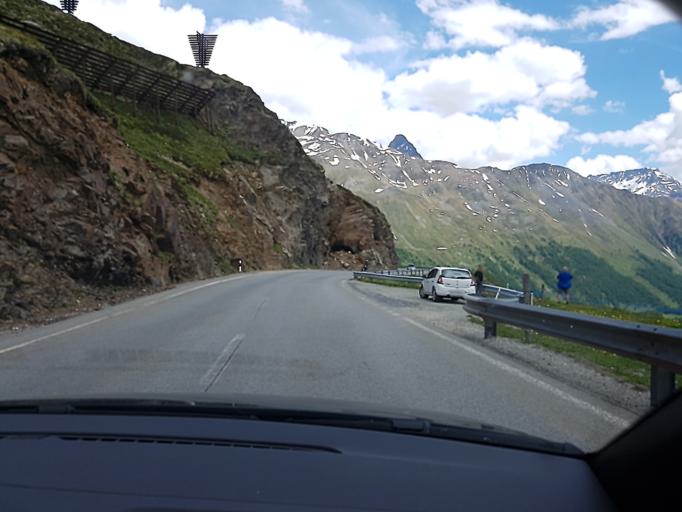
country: CH
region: Grisons
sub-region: Bernina District
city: Poschiavo
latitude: 46.4114
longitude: 10.0309
